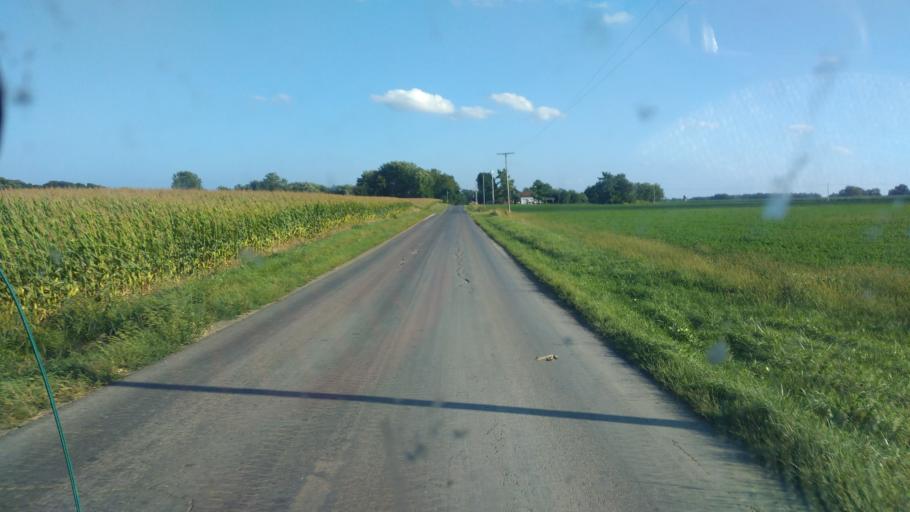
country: US
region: Ohio
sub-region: Huron County
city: Greenwich
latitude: 40.9417
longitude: -82.4532
